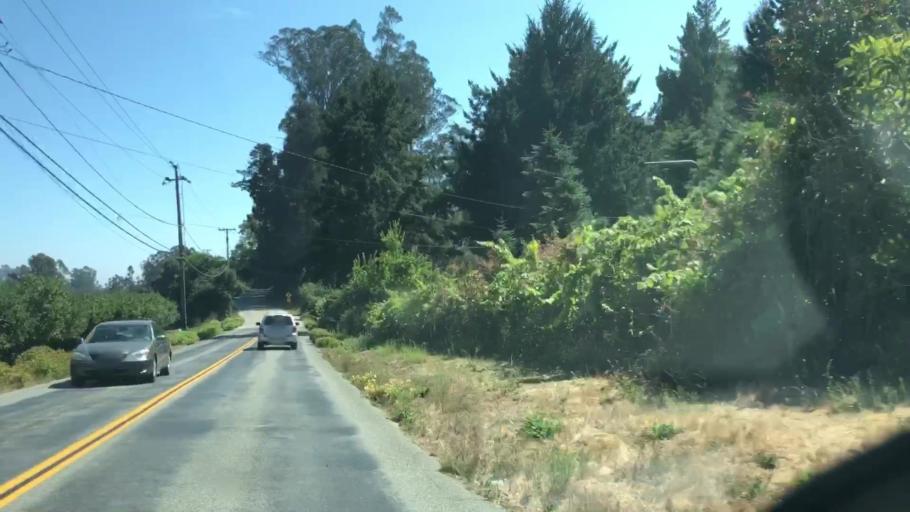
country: US
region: California
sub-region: Santa Cruz County
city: Corralitos
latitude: 36.9957
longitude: -121.8049
